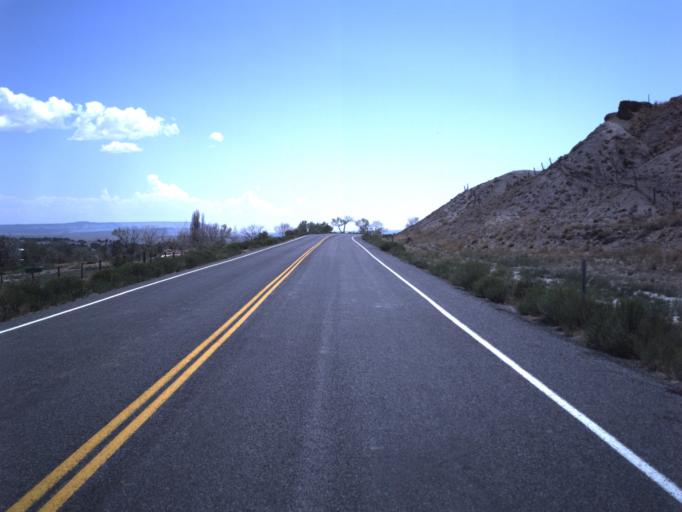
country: US
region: Utah
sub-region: Emery County
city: Orangeville
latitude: 39.2149
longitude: -111.0621
